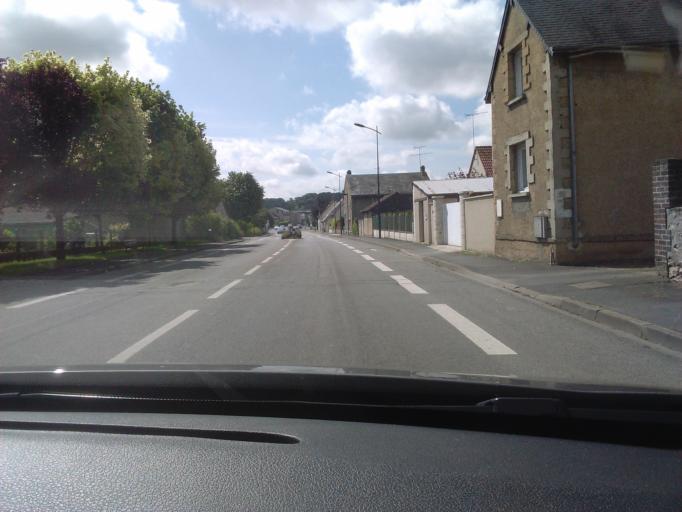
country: FR
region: Centre
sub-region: Departement du Loir-et-Cher
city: Vendome
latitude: 47.7992
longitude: 1.0581
